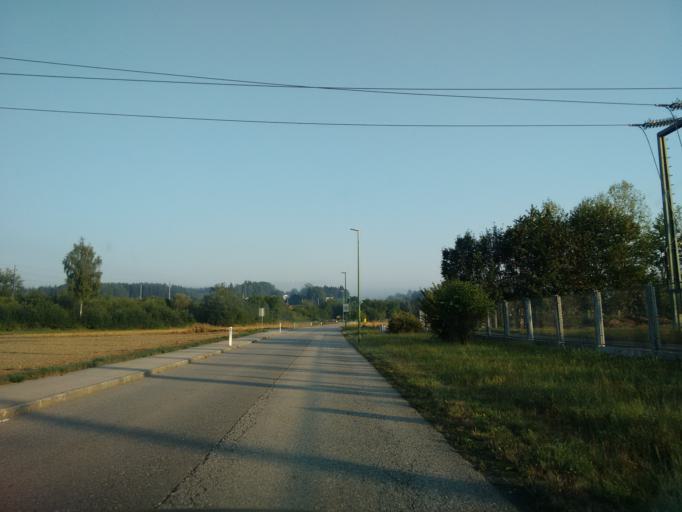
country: AT
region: Upper Austria
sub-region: Wels Stadt
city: Wels
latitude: 48.1840
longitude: 14.0044
